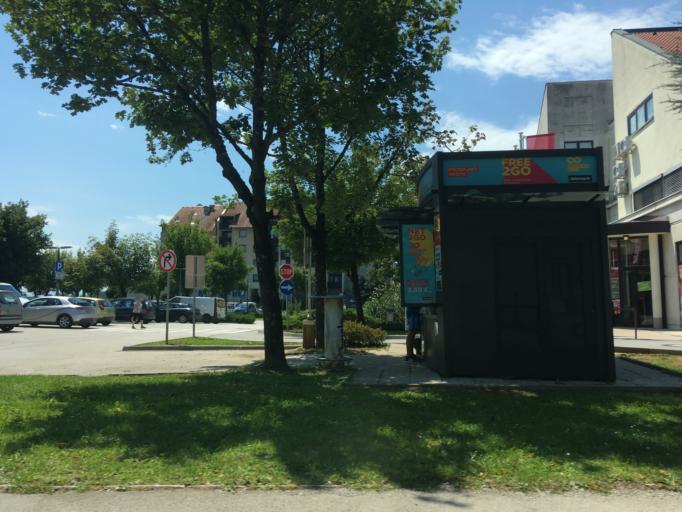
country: SI
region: Metlika
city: Metlika
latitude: 45.6457
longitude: 15.3176
